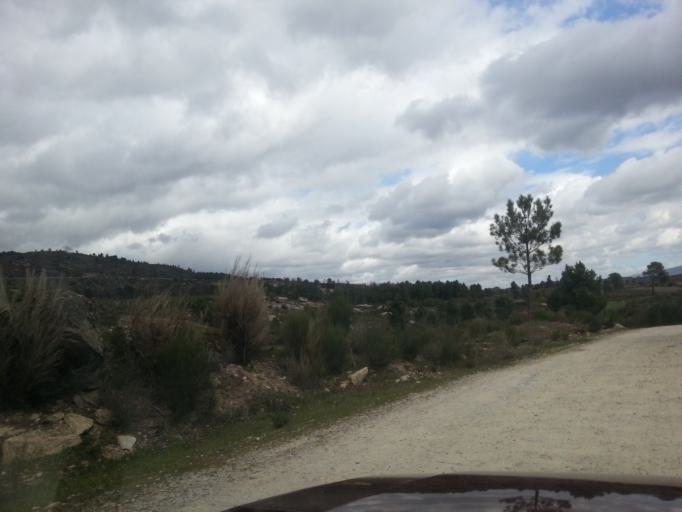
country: PT
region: Guarda
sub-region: Fornos de Algodres
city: Fornos de Algodres
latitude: 40.5990
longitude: -7.5653
